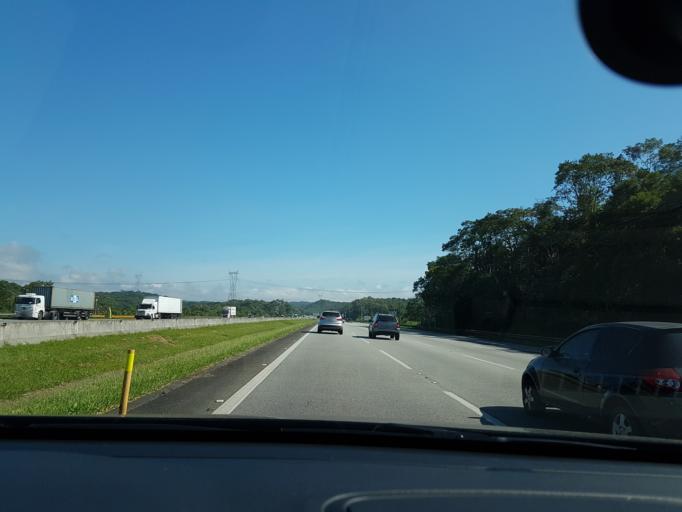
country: BR
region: Sao Paulo
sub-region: Cubatao
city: Cubatao
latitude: -23.8544
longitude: -46.5742
